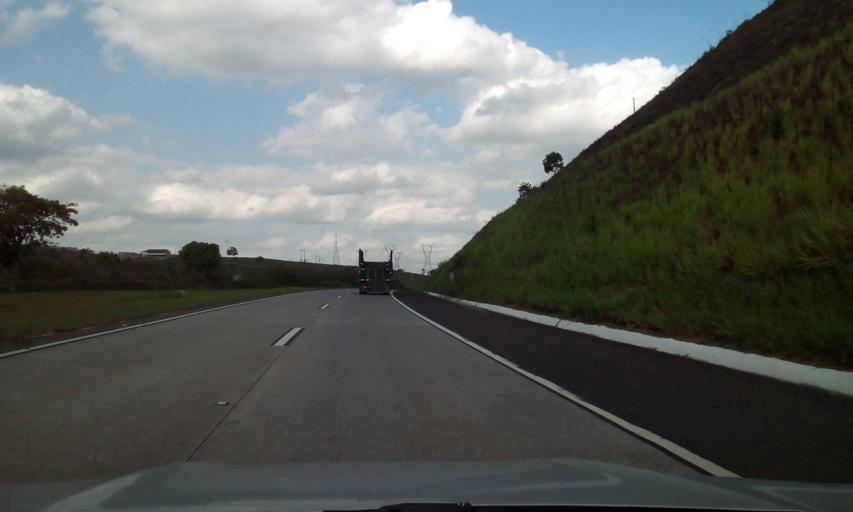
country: BR
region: Pernambuco
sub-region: Joaquim Nabuco
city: Joaquim Nabuco
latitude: -8.5942
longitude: -35.5241
